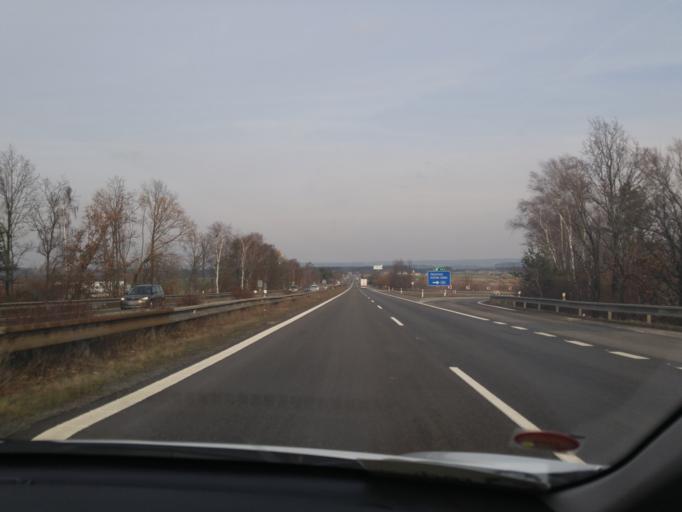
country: CZ
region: Central Bohemia
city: Cechtice
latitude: 49.6557
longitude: 15.1222
